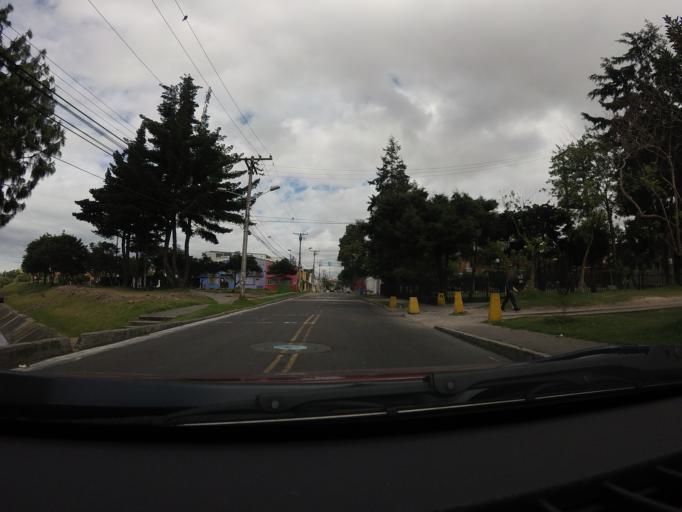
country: CO
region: Bogota D.C.
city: Bogota
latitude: 4.6342
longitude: -74.1417
